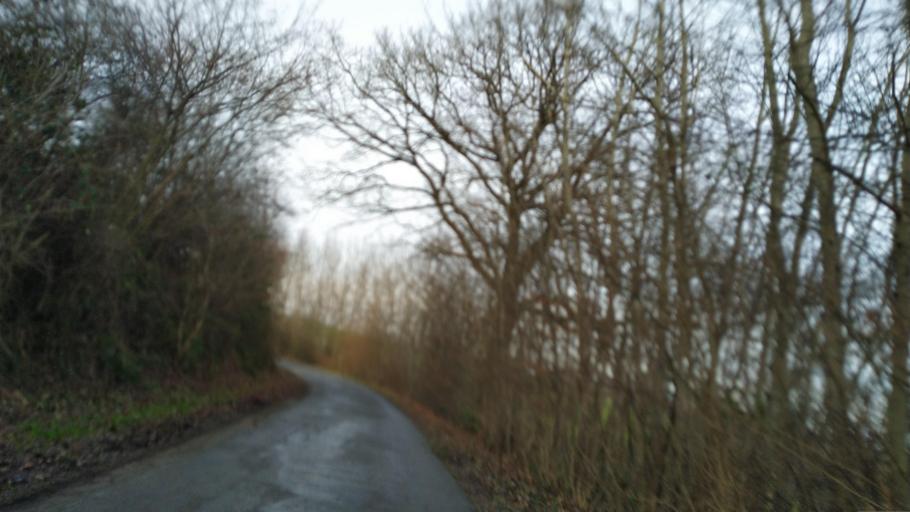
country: DE
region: Schleswig-Holstein
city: Neukirchen
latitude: 54.2001
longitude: 10.5976
